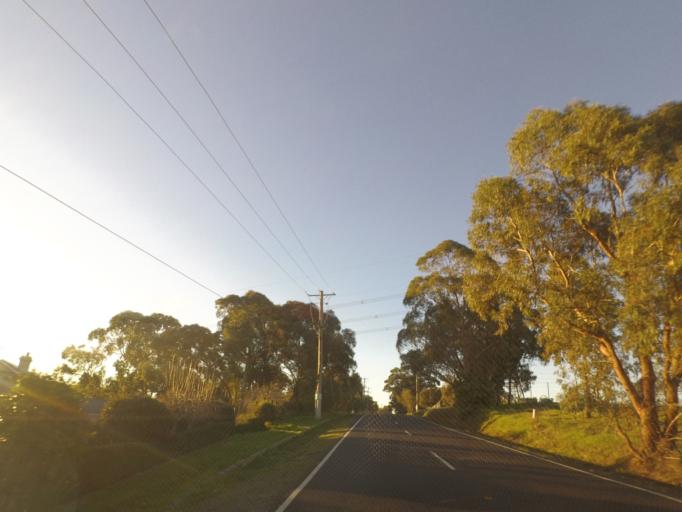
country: AU
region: Victoria
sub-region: Manningham
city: Park Orchards
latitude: -37.7606
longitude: 145.1963
